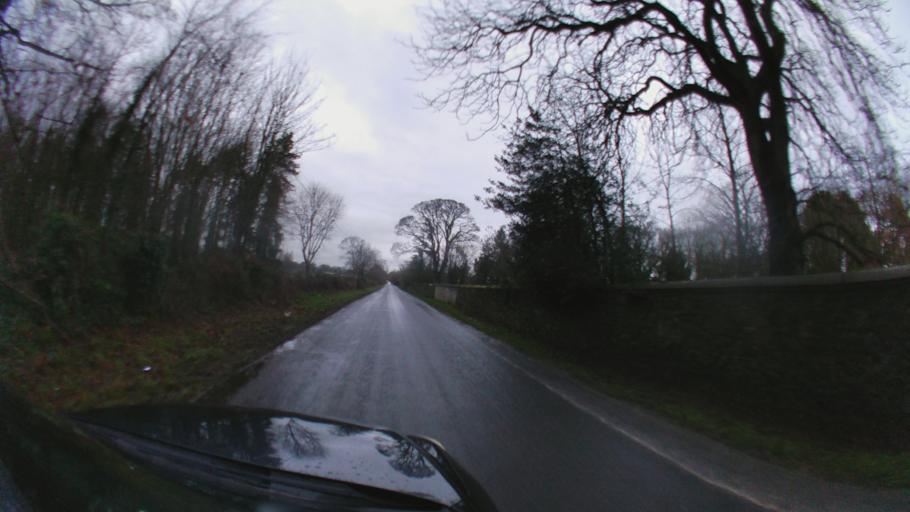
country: IE
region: Leinster
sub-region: County Carlow
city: Bagenalstown
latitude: 52.6490
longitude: -6.9888
